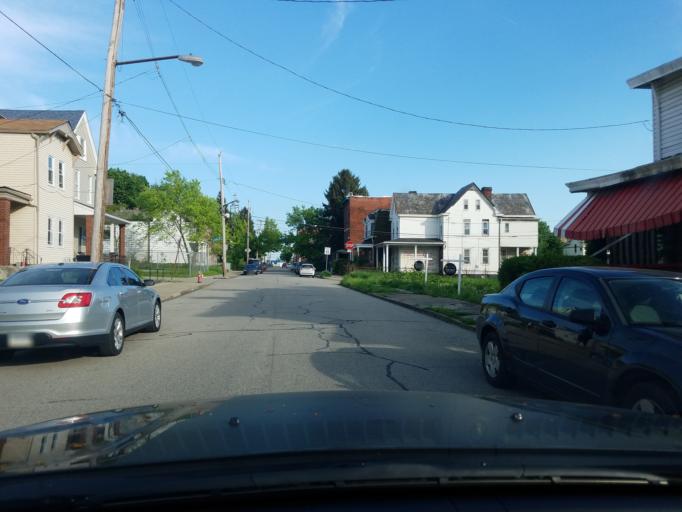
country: US
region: Pennsylvania
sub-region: Allegheny County
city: Aspinwall
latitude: 40.4633
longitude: -79.9155
